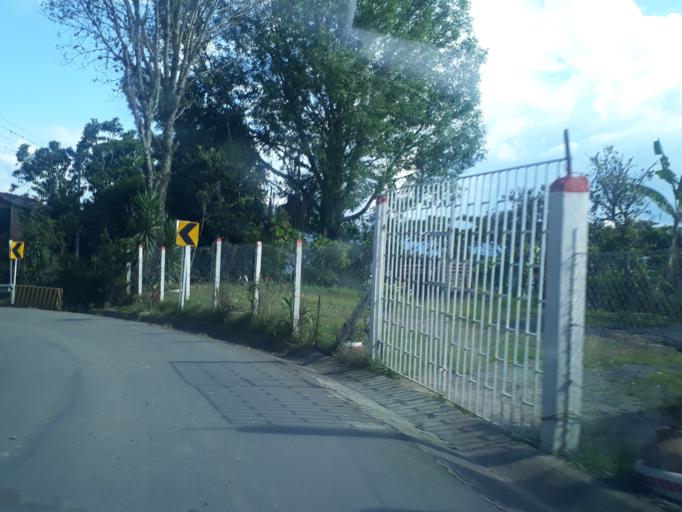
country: CO
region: Santander
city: Velez
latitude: 6.0205
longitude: -73.6630
